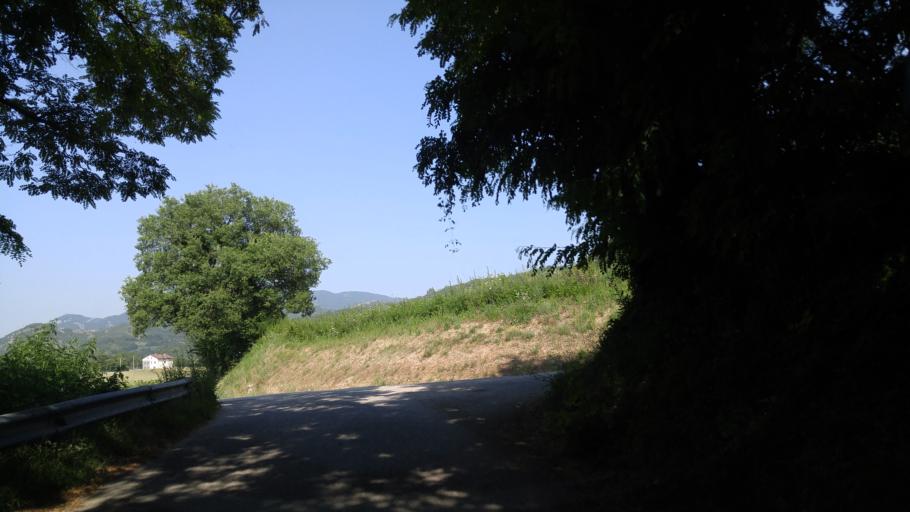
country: IT
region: The Marches
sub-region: Provincia di Pesaro e Urbino
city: Acqualagna
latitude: 43.6119
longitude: 12.6636
